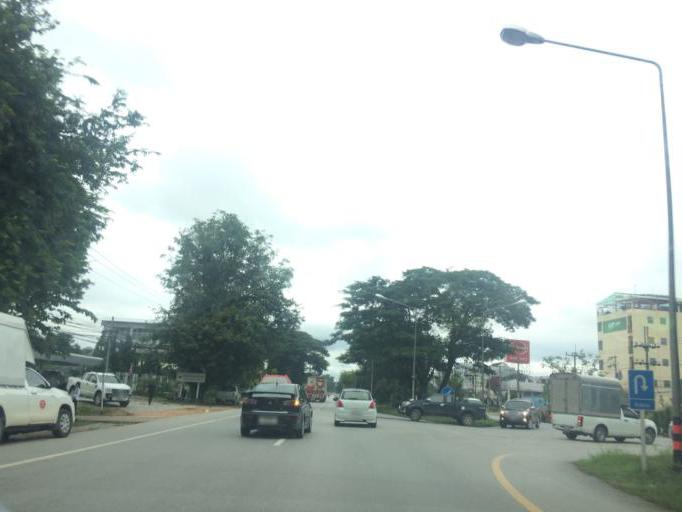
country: TH
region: Chiang Rai
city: Chiang Rai
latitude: 19.8638
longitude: 99.8220
